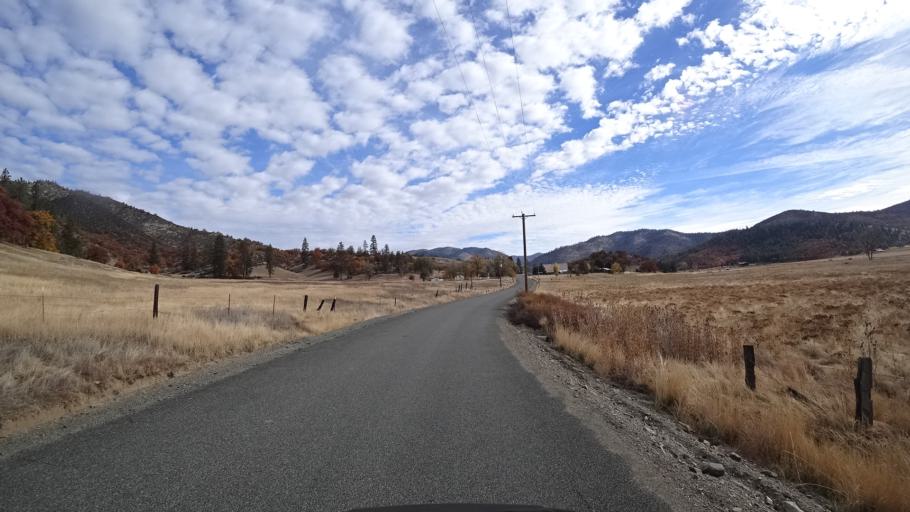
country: US
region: California
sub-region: Siskiyou County
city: Yreka
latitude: 41.6239
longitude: -122.7899
